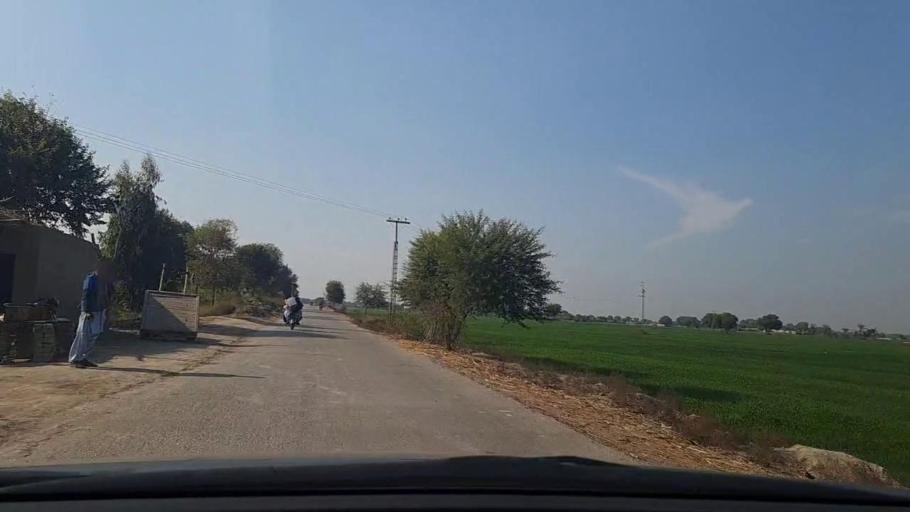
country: PK
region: Sindh
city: Daulatpur
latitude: 26.3116
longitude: 68.0747
